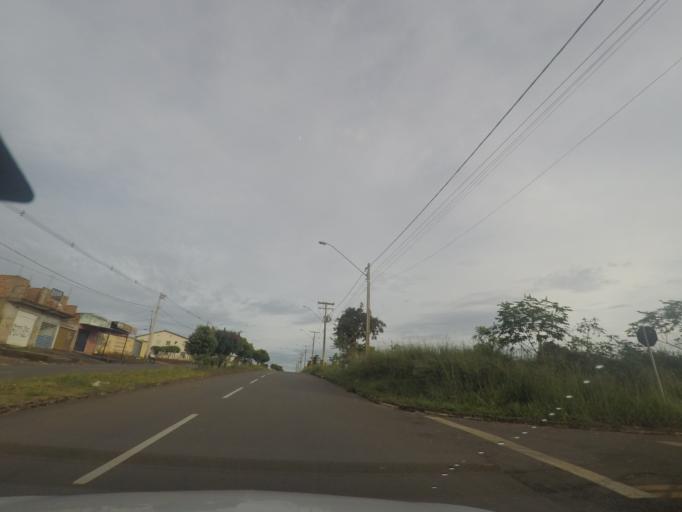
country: BR
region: Goias
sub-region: Trindade
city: Trindade
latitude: -16.7282
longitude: -49.4029
